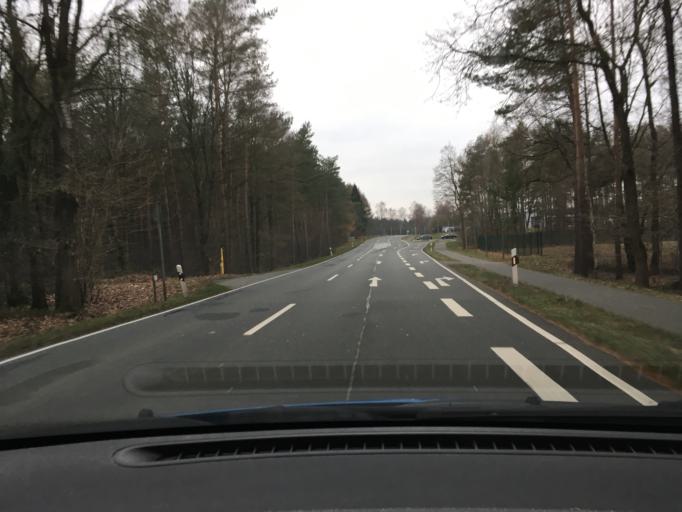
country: DE
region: Lower Saxony
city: Soltau
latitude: 52.9685
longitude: 9.8191
